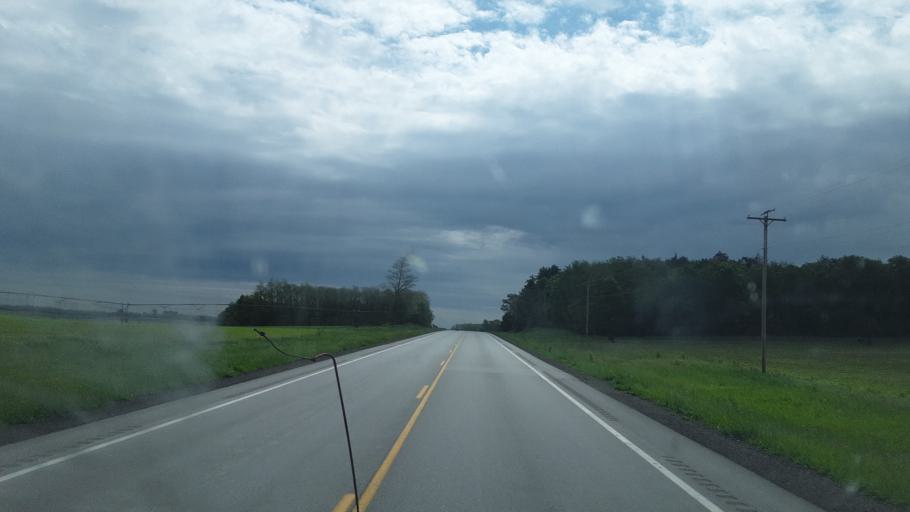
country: US
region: Illinois
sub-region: Mason County
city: Havana
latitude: 40.2976
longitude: -89.9416
